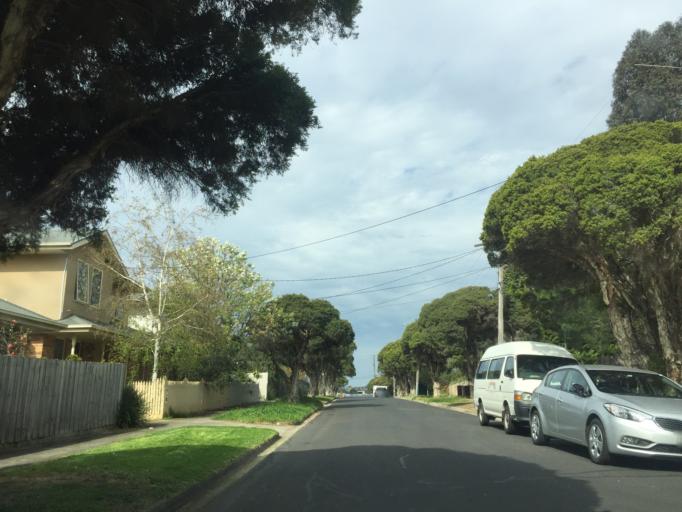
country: AU
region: Victoria
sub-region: Darebin
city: Preston
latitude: -37.7520
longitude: 145.0193
